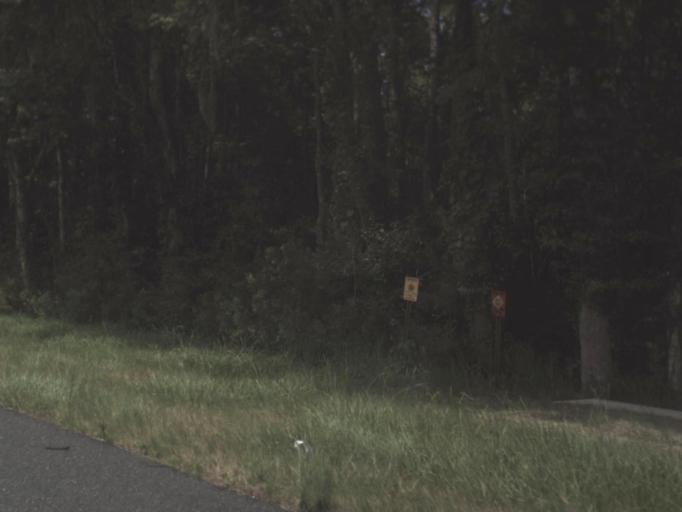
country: US
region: Florida
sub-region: Taylor County
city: Perry
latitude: 30.2558
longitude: -83.7049
